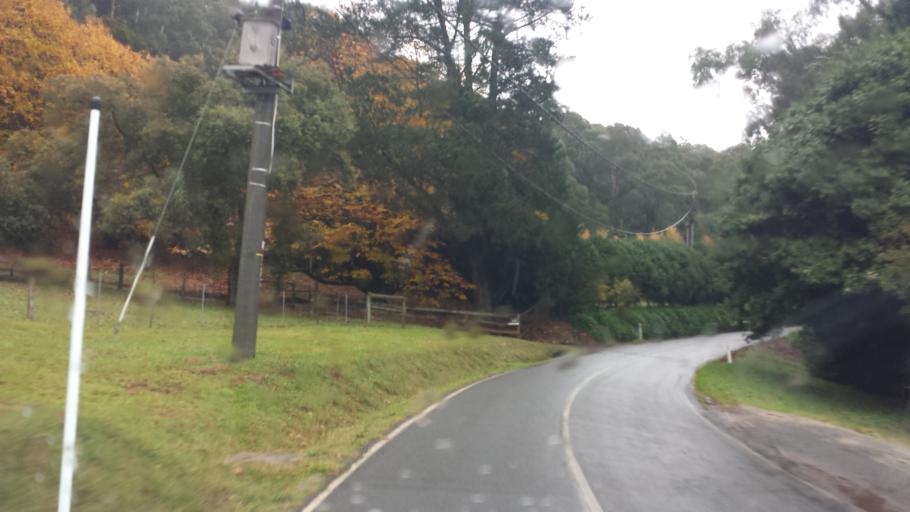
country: AU
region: Victoria
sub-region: Yarra Ranges
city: Monbulk
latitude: -37.9006
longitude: 145.4101
